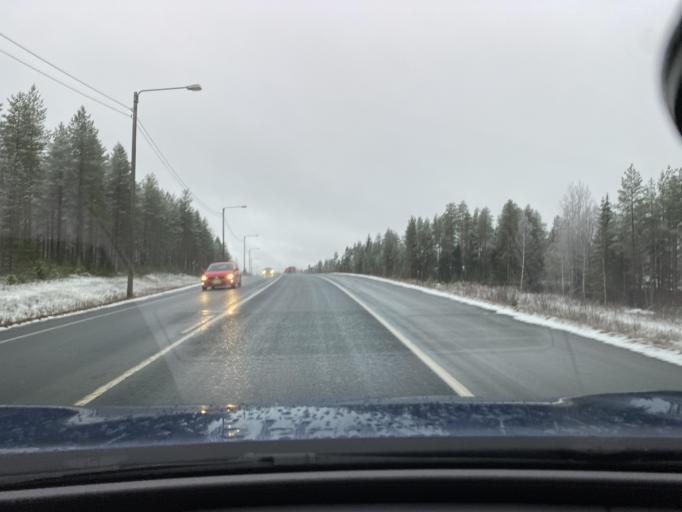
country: FI
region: Northern Ostrobothnia
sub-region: Oulu
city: Kiiminki
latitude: 65.1234
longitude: 25.7567
